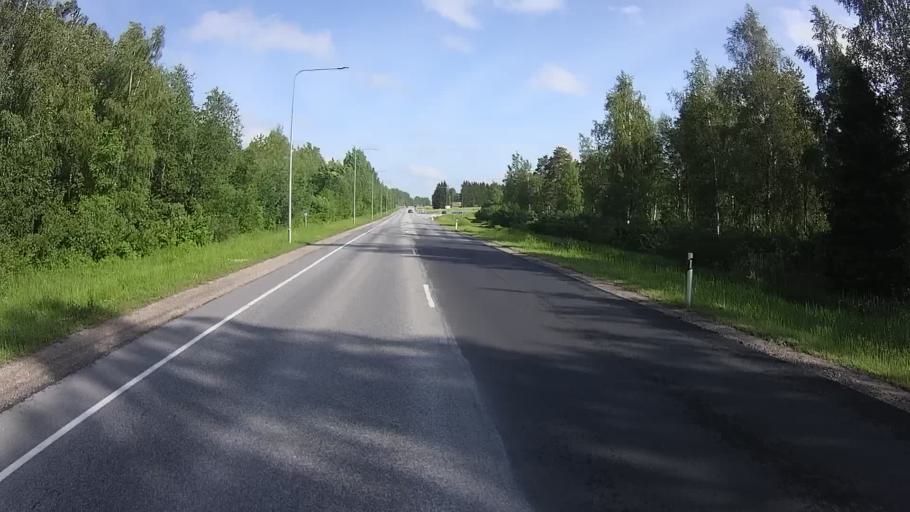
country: EE
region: Viljandimaa
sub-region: Viljandi linn
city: Viljandi
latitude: 58.3347
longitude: 25.5727
